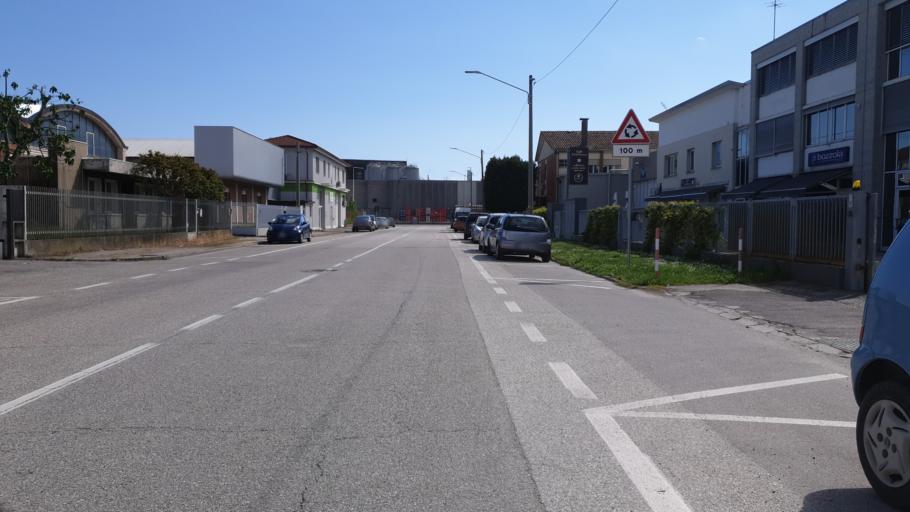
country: IT
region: Veneto
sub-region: Provincia di Padova
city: Noventa
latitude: 45.4137
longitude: 11.9302
